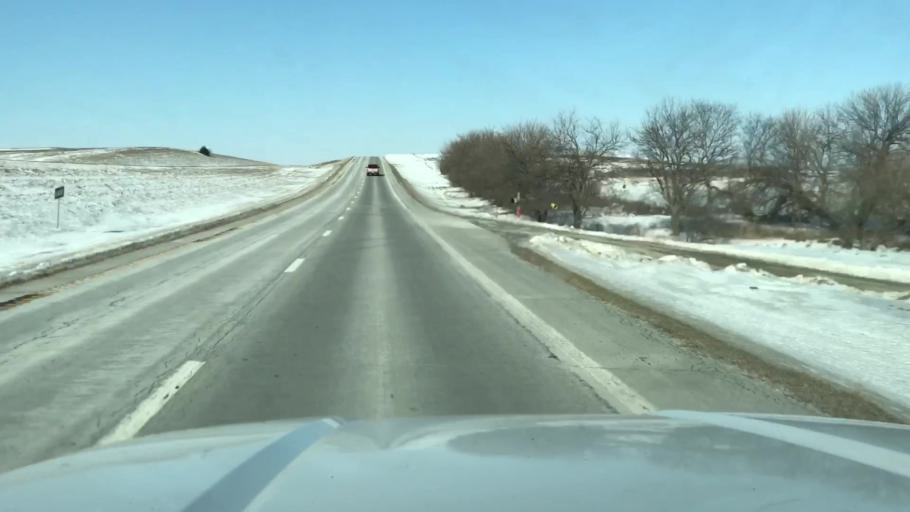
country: US
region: Missouri
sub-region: Andrew County
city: Savannah
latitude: 39.9704
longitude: -94.8710
